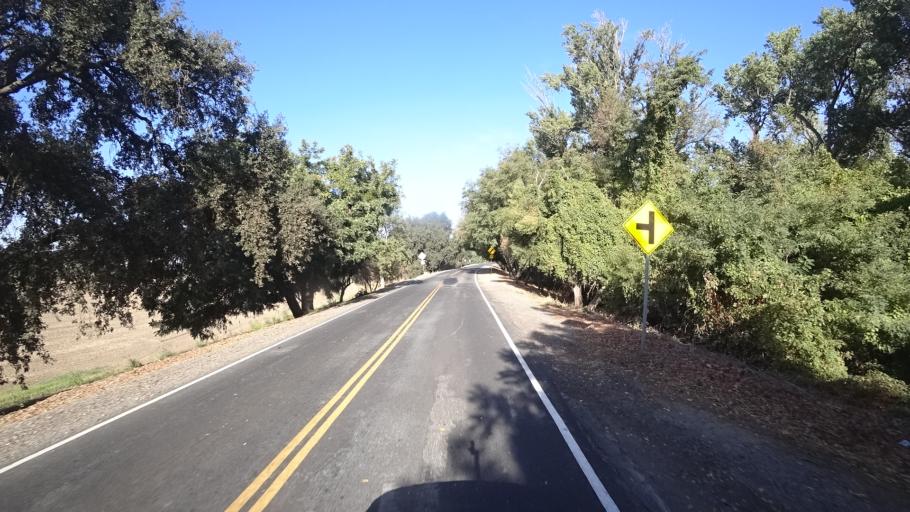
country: US
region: California
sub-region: Sacramento County
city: Parkway
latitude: 38.4786
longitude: -121.5478
